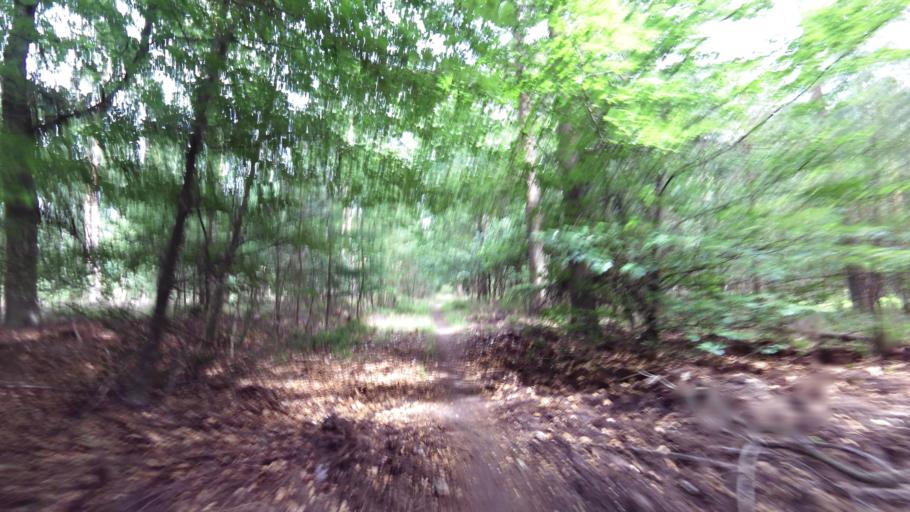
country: NL
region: Gelderland
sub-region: Gemeente Apeldoorn
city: Apeldoorn
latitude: 52.1918
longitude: 5.9103
